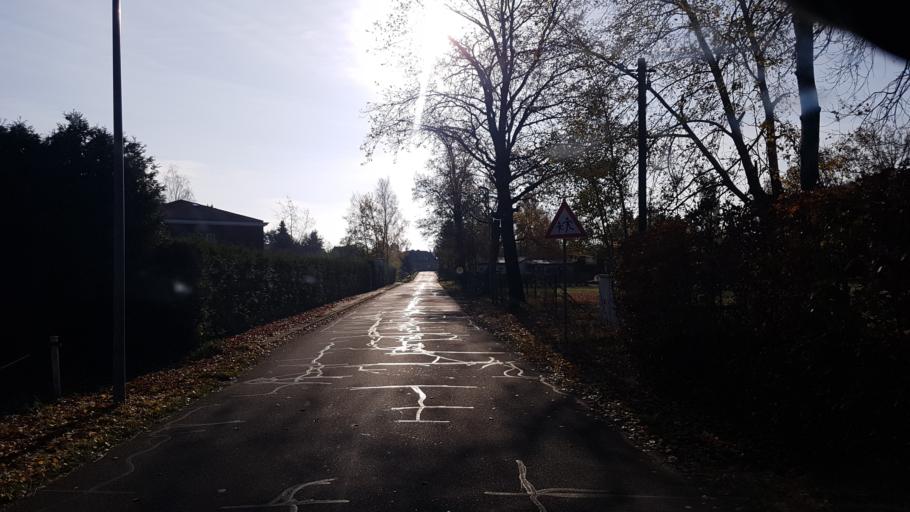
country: DE
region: Brandenburg
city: Schipkau
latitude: 51.5531
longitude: 13.9293
